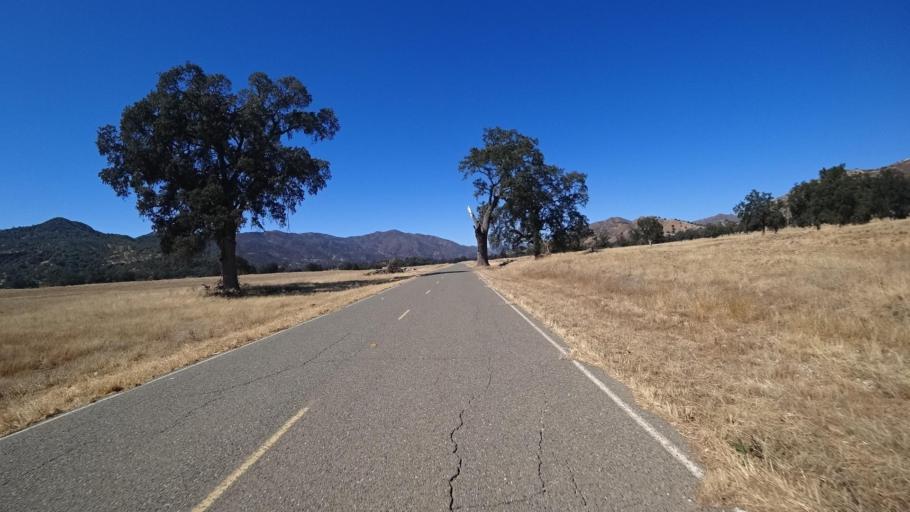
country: US
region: California
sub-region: Monterey County
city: King City
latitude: 35.9672
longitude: -121.3126
